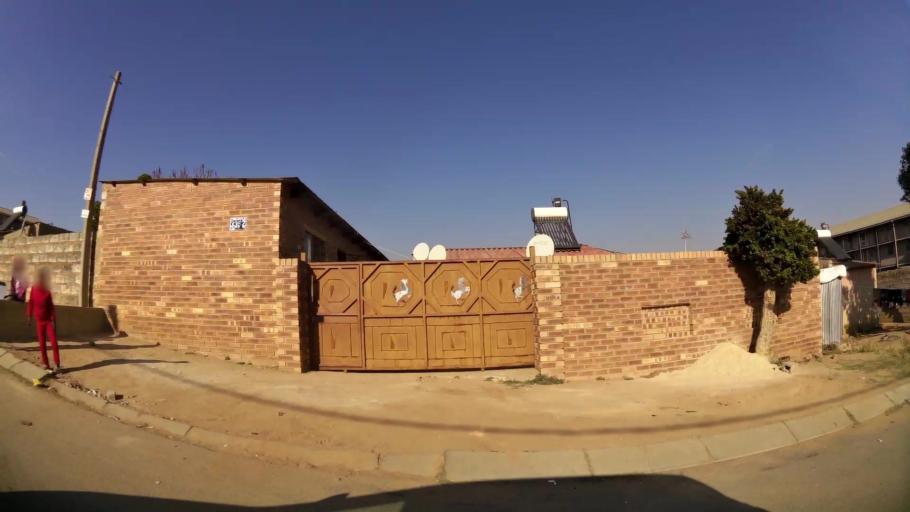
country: ZA
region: Gauteng
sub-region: City of Johannesburg Metropolitan Municipality
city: Modderfontein
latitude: -26.0964
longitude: 28.1122
